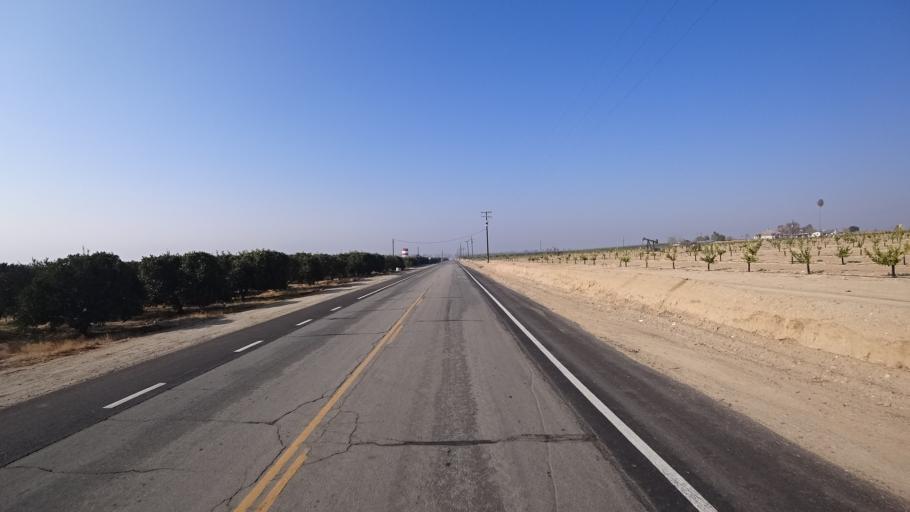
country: US
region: California
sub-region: Kern County
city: Lamont
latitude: 35.3618
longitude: -118.8747
